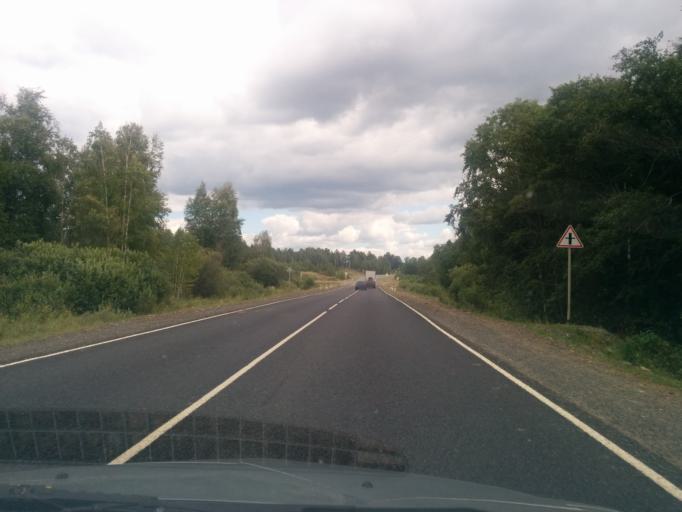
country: RU
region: Bashkortostan
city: Lomovka
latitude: 53.8971
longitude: 58.0844
